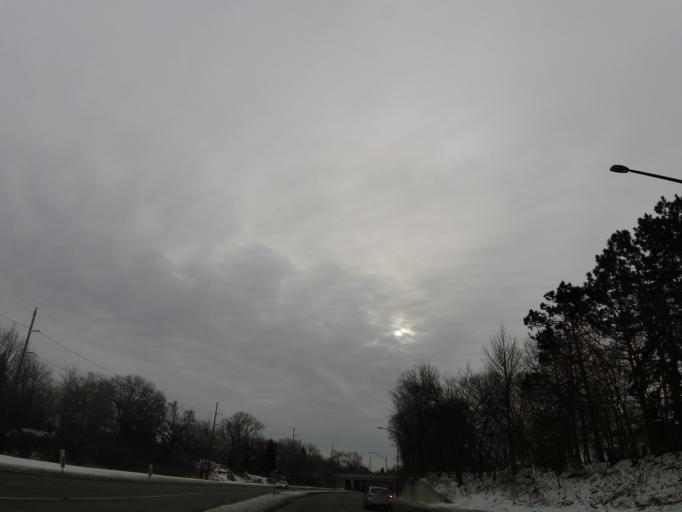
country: US
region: Minnesota
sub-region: Ramsey County
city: Falcon Heights
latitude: 44.9435
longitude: -93.1546
